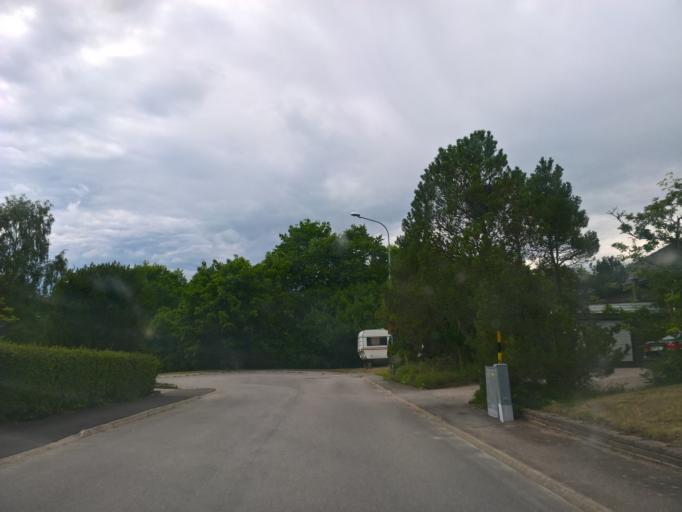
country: SE
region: OEstergoetland
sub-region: Finspangs Kommun
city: Finspang
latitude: 58.7392
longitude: 15.8295
